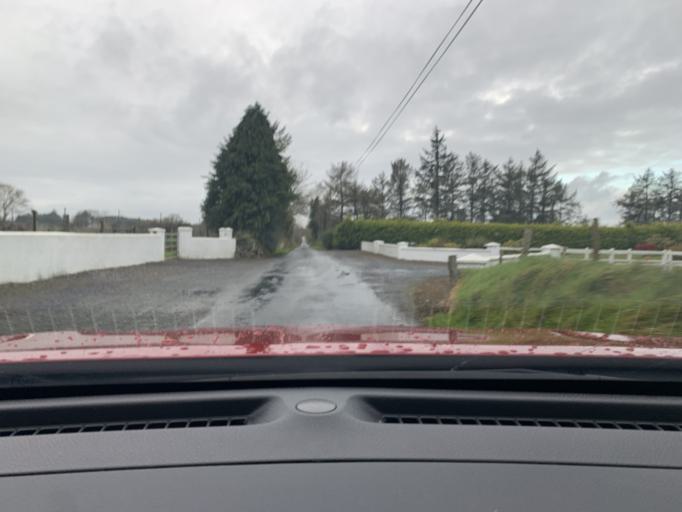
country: IE
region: Connaught
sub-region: Roscommon
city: Ballaghaderreen
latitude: 53.9664
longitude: -8.5613
